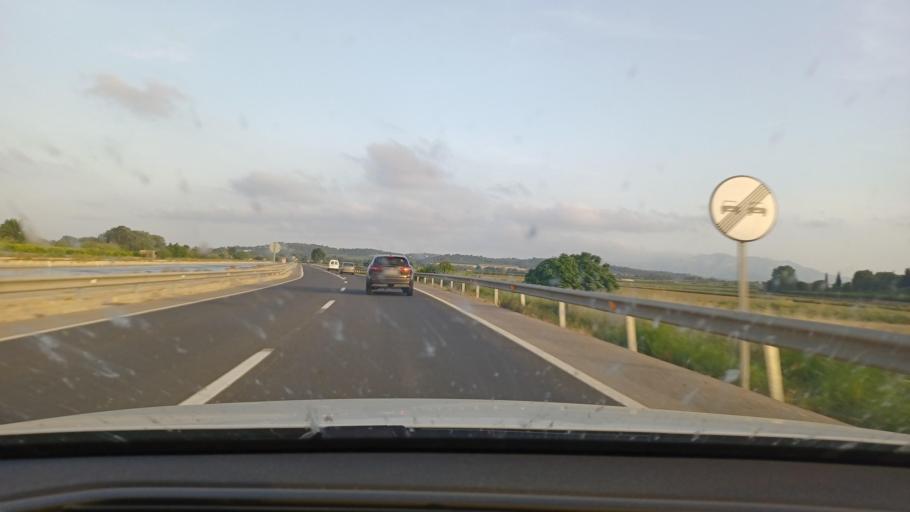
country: ES
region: Catalonia
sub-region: Provincia de Tarragona
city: Masdenverge
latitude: 40.7596
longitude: 0.5344
